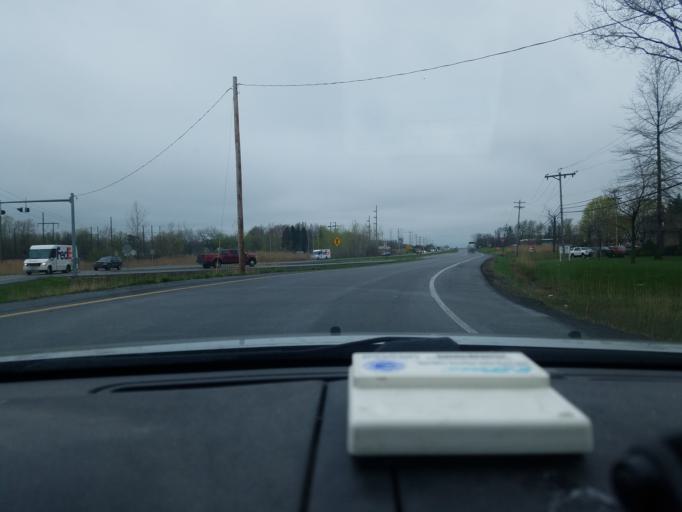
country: US
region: New York
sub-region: Onondaga County
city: East Syracuse
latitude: 43.1005
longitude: -76.0765
